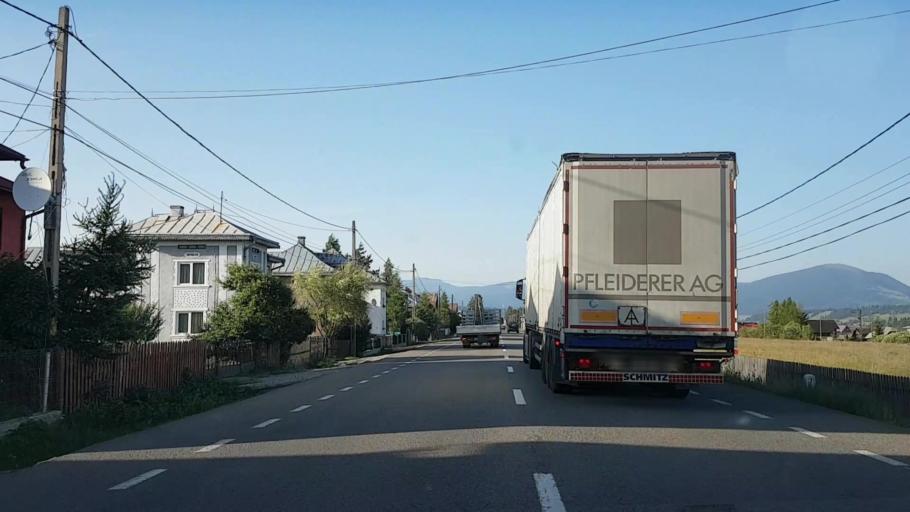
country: RO
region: Suceava
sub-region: Comuna Poiana Stampei
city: Poiana Stampei
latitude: 47.3139
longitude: 25.1311
